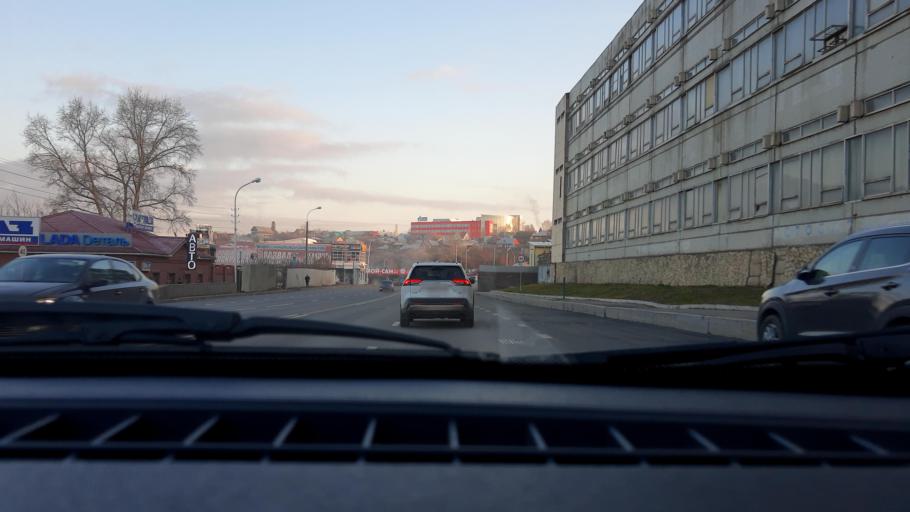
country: RU
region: Bashkortostan
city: Ufa
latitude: 54.7470
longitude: 55.9715
